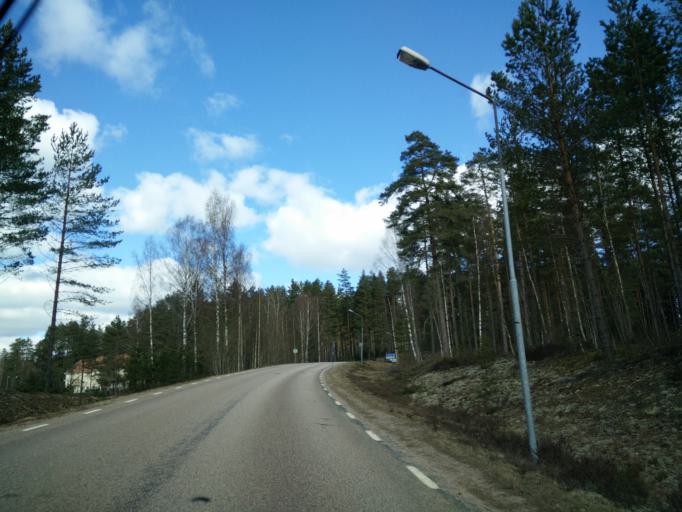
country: SE
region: Vaermland
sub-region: Hagfors Kommun
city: Hagfors
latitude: 59.8859
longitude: 13.7136
